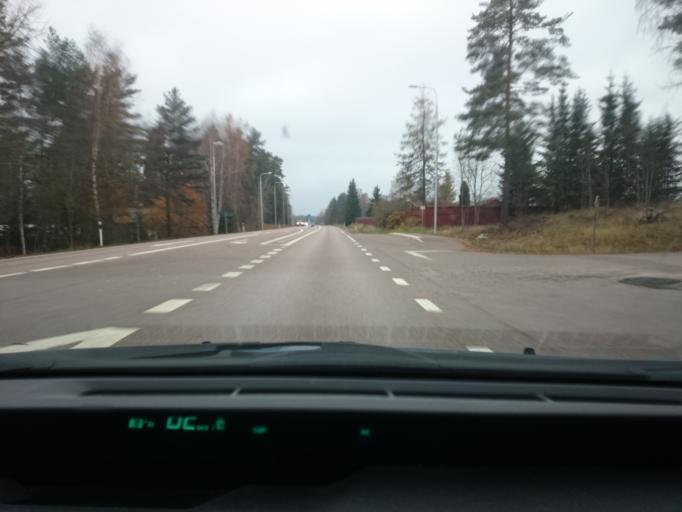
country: SE
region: Dalarna
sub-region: Avesta Kommun
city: Avesta
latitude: 60.1818
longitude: 16.1299
